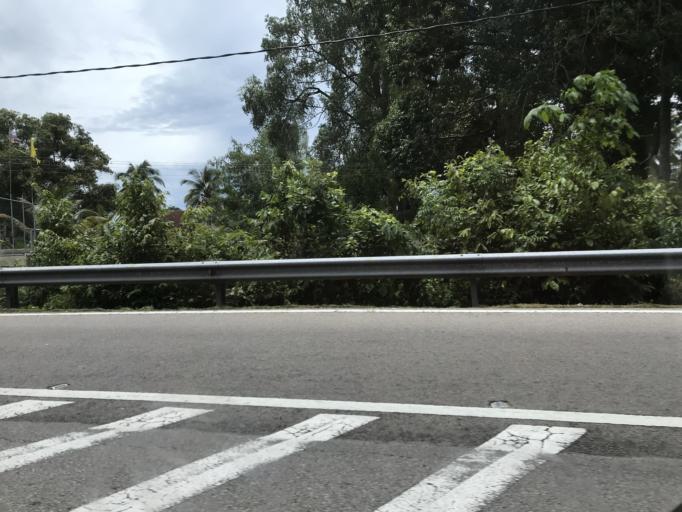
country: MY
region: Kelantan
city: Tumpat
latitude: 6.1751
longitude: 102.1997
